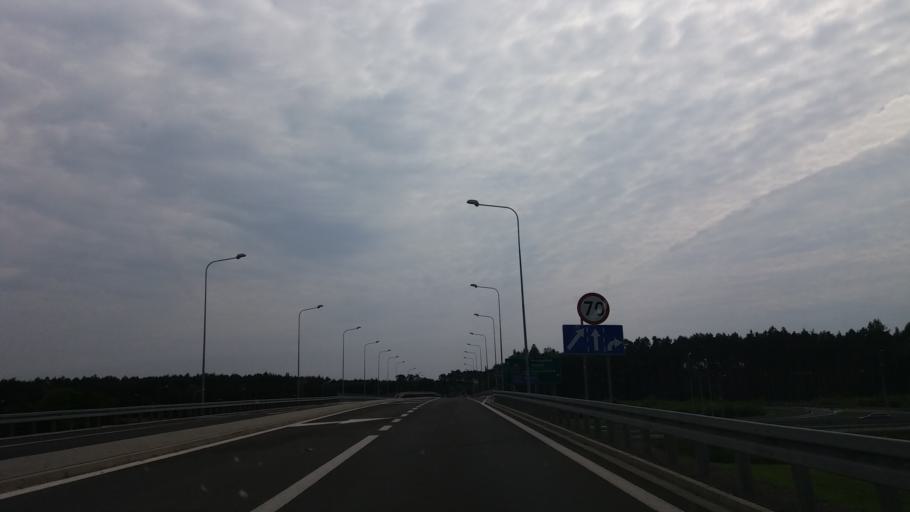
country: PL
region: Lubusz
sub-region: Powiat miedzyrzecki
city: Skwierzyna
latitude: 52.5620
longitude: 15.5244
